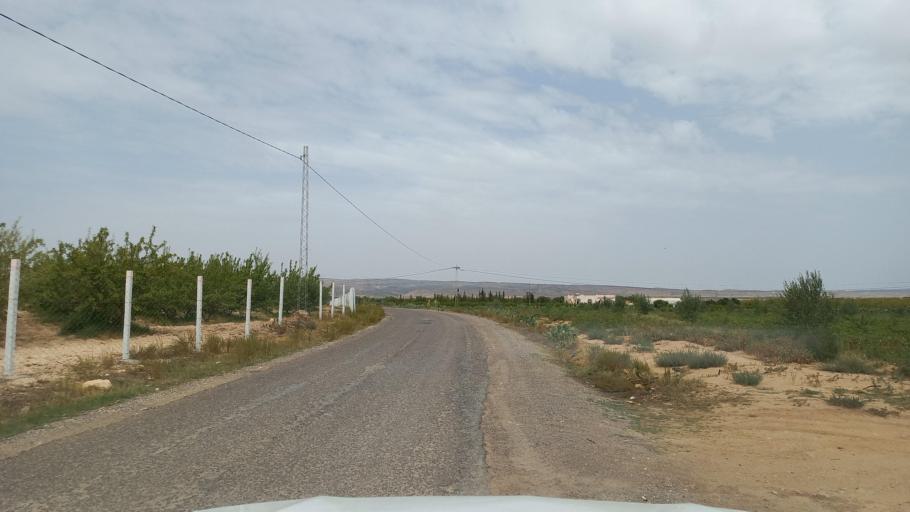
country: TN
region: Al Qasrayn
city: Kasserine
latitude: 35.2641
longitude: 9.0076
